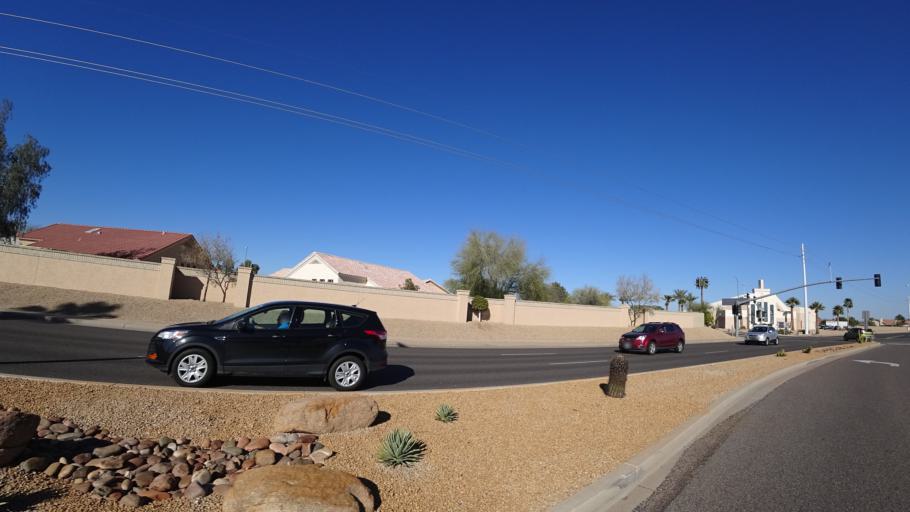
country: US
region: Arizona
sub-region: Maricopa County
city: Sun City West
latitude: 33.6724
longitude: -112.3803
